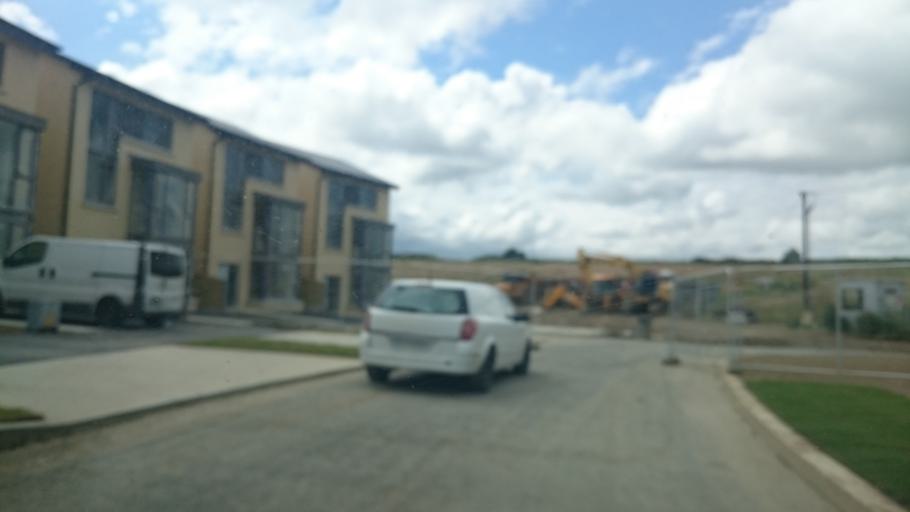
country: IE
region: Leinster
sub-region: Fingal County
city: Skerries
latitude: 53.5851
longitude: -6.1414
